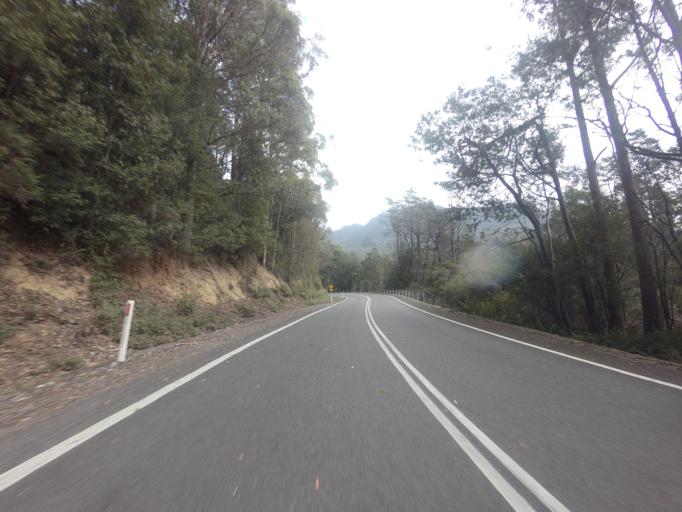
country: AU
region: Tasmania
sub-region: Meander Valley
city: Deloraine
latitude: -41.6463
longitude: 146.7217
